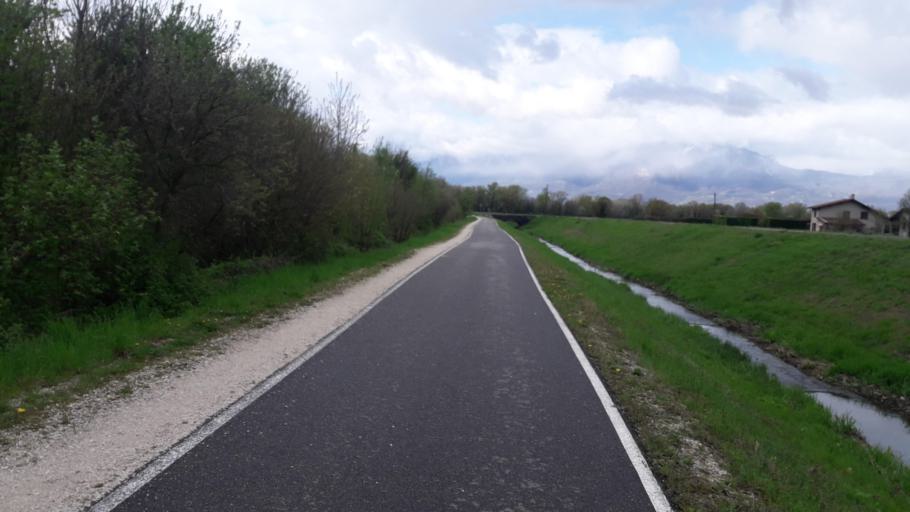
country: FR
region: Rhone-Alpes
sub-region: Departement de l'Isere
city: Gieres
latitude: 45.1951
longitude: 5.8123
